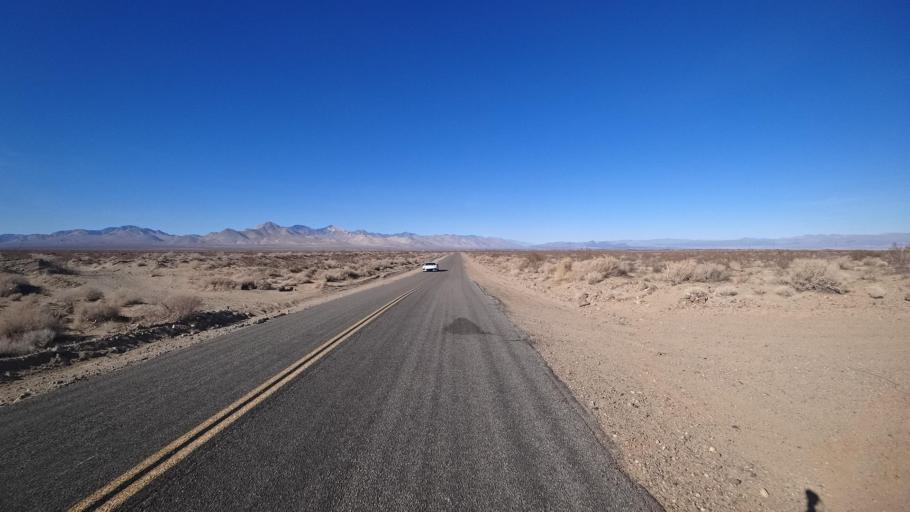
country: US
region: California
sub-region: Kern County
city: China Lake Acres
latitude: 35.5714
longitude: -117.7815
